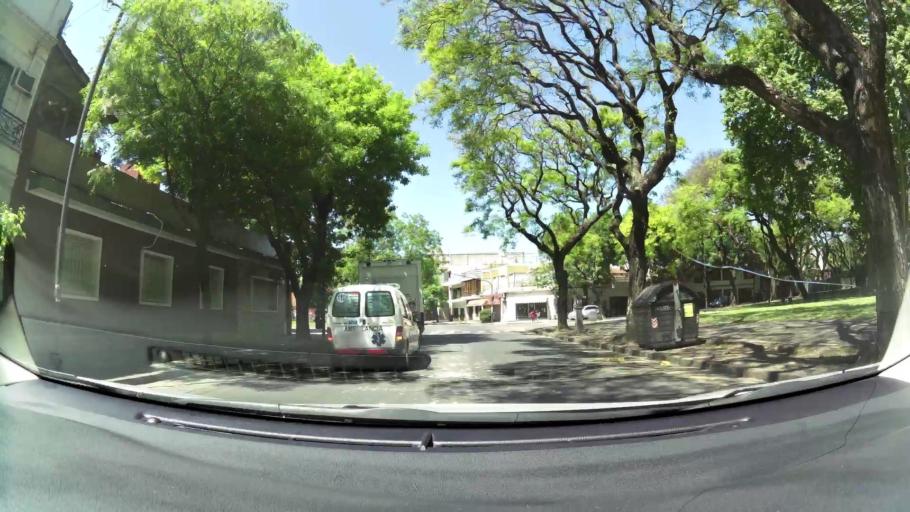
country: AR
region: Buenos Aires
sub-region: Partido de Avellaneda
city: Avellaneda
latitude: -34.6447
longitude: -58.4096
